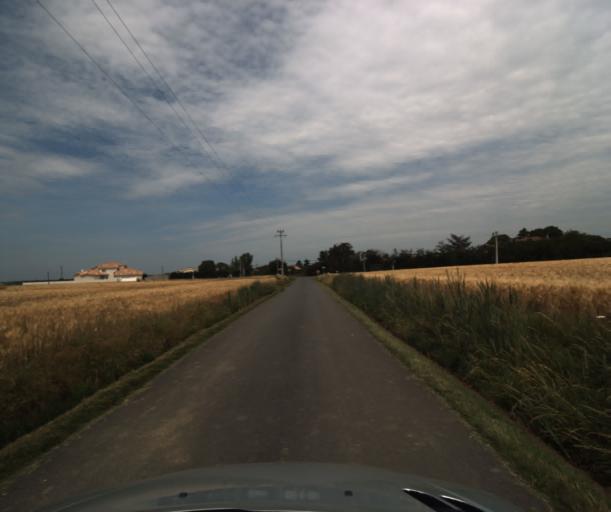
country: FR
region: Midi-Pyrenees
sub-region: Departement de la Haute-Garonne
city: Lacasse
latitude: 43.4141
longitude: 1.2750
